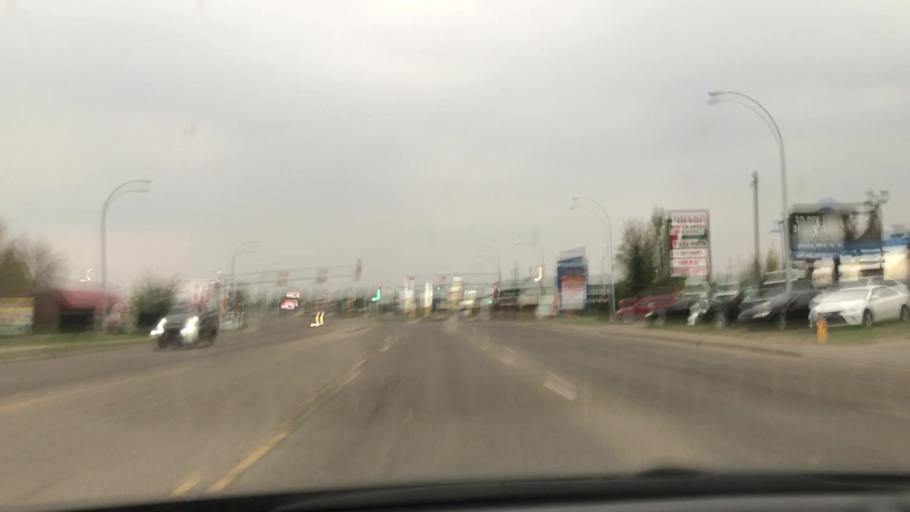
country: CA
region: Alberta
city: Edmonton
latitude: 53.4664
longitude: -113.4767
